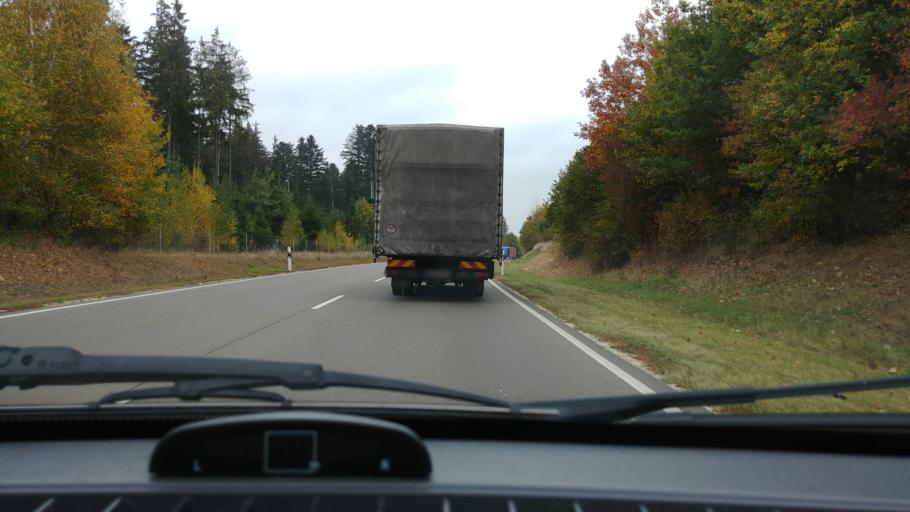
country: DE
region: Baden-Wuerttemberg
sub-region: Regierungsbezirk Stuttgart
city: Huttlingen
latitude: 48.8771
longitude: 10.0800
